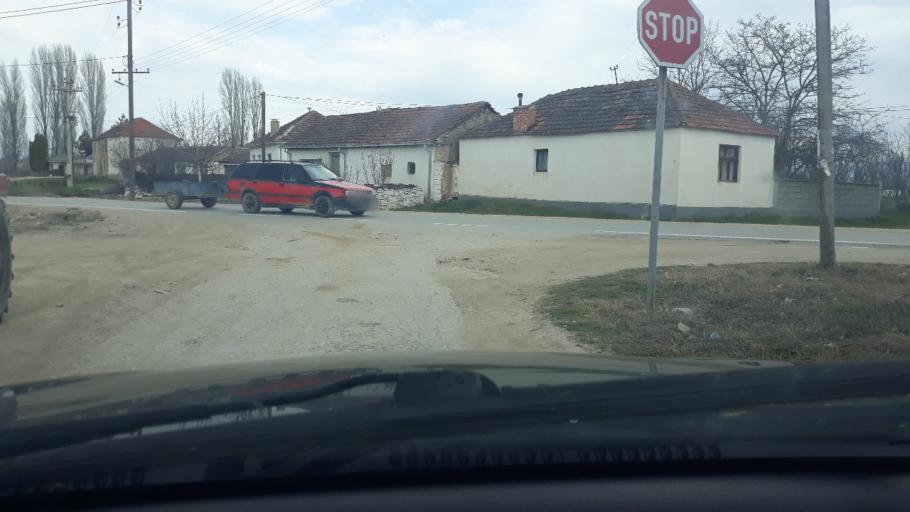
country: MK
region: Krivogastani
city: Obrsani
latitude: 41.2823
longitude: 21.3399
